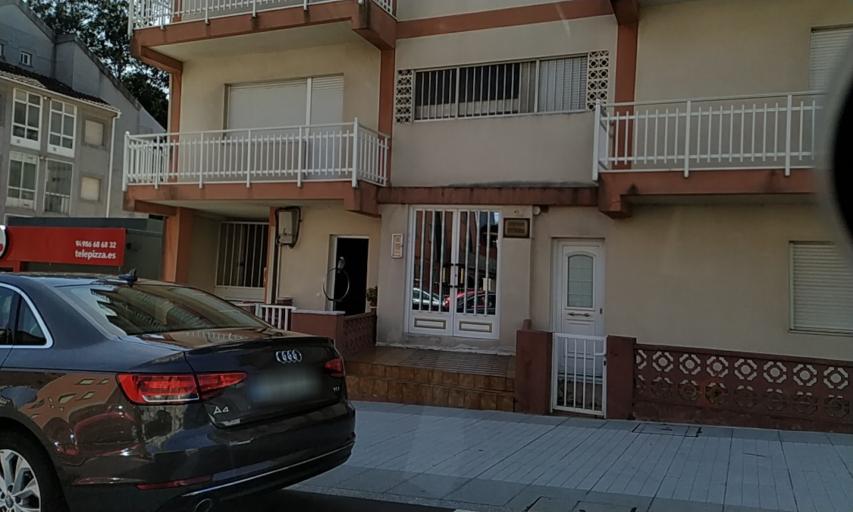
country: ES
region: Galicia
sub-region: Provincia de Pontevedra
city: Sanxenxo
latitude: 42.4061
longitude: -8.8125
